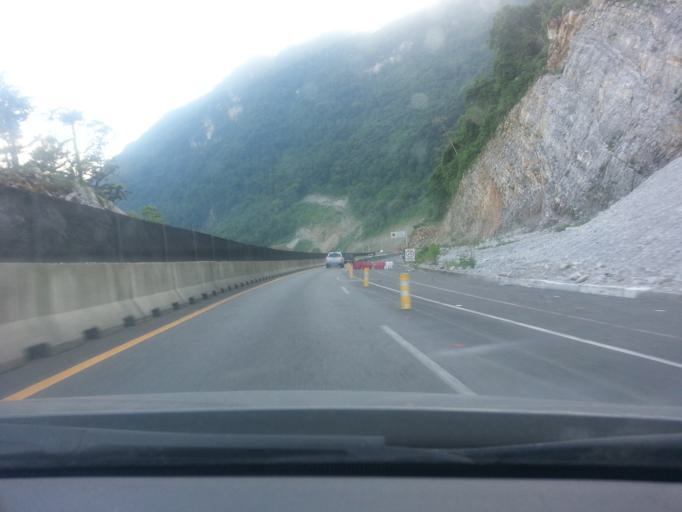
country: MX
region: Puebla
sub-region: Xicotepec
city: San Lorenzo
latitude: 20.3637
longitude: -97.9593
